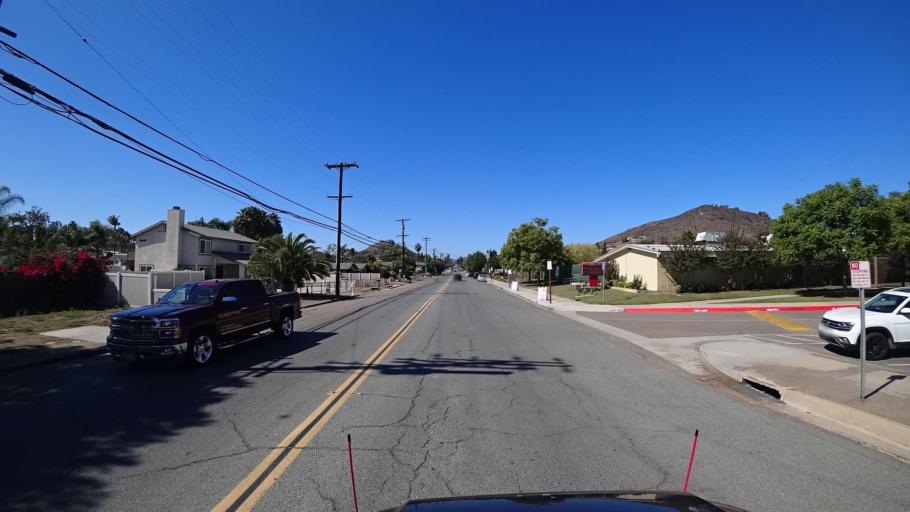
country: US
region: California
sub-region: San Diego County
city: Winter Gardens
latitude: 32.8209
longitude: -116.9305
